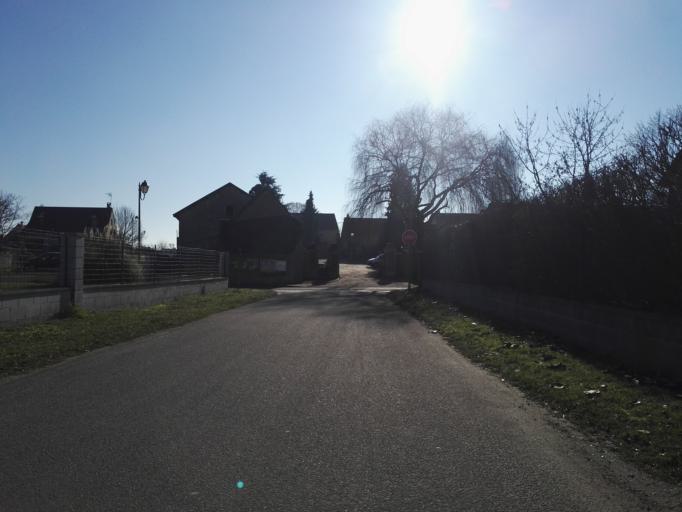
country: FR
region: Haute-Normandie
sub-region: Departement de l'Eure
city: Pacy-sur-Eure
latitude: 49.0070
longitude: 1.4191
